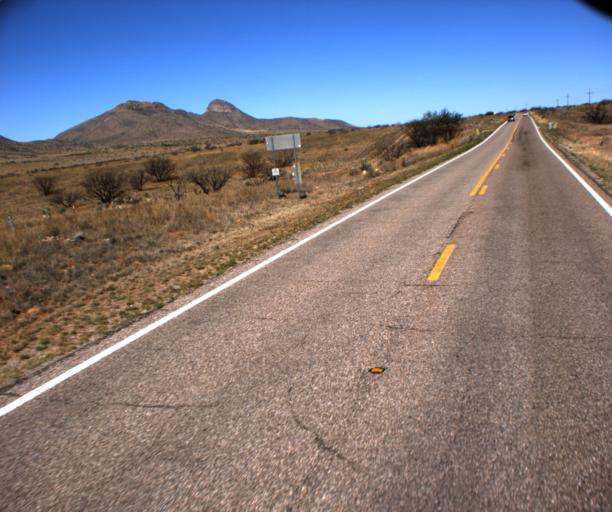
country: US
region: Arizona
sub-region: Cochise County
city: Huachuca City
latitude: 31.7064
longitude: -110.4408
